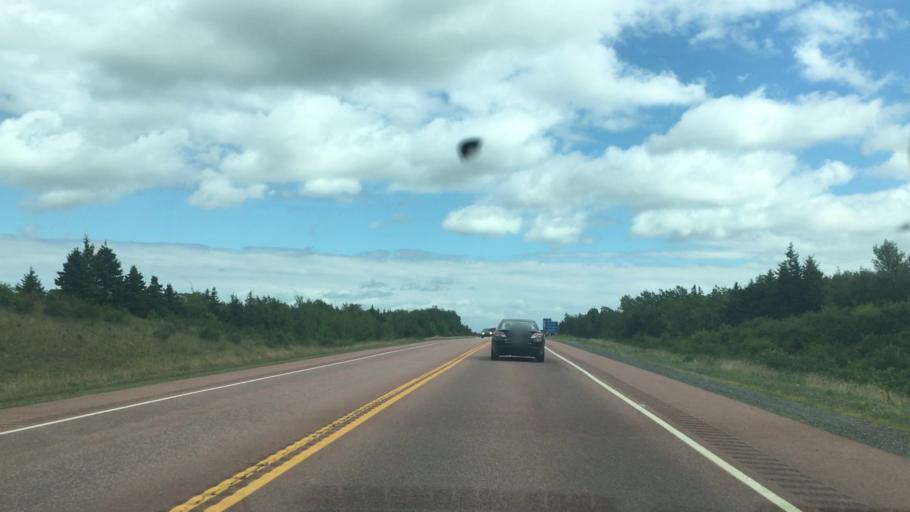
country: CA
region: Nova Scotia
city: Port Hawkesbury
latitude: 45.6065
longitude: -61.6714
